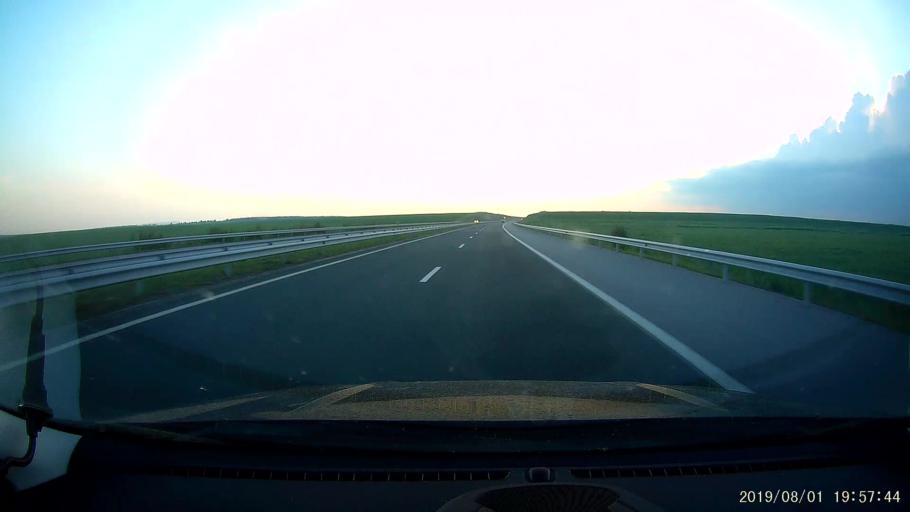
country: BG
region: Yambol
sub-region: Obshtina Straldzha
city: Straldzha
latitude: 42.5489
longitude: 26.7897
